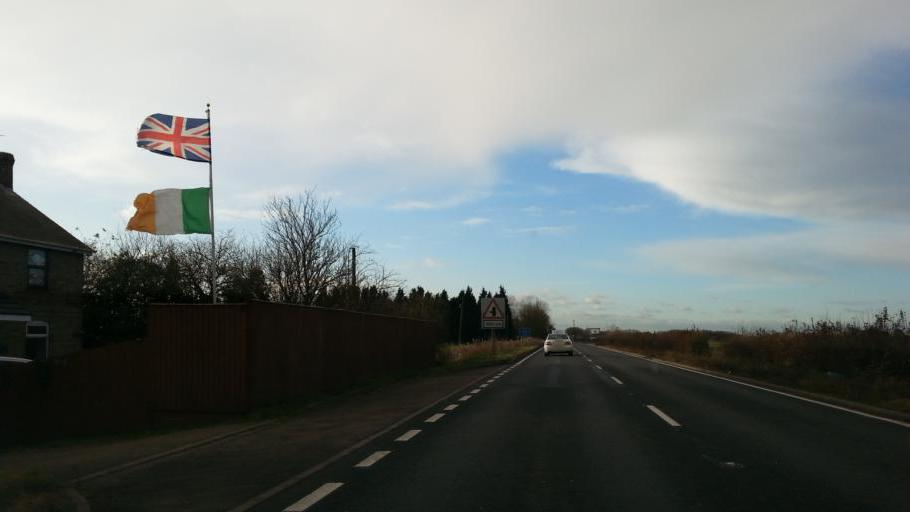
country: GB
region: England
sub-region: Peterborough
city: Thorney
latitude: 52.6197
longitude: -0.0449
